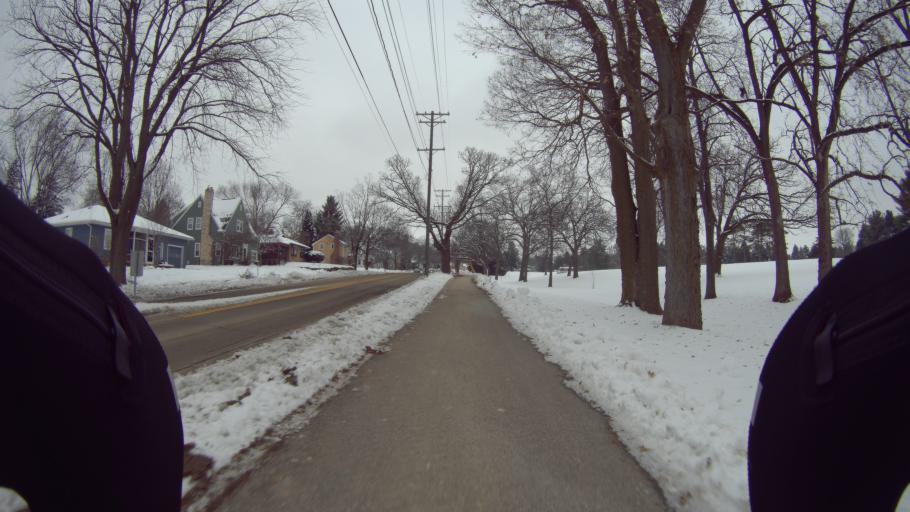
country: US
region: Wisconsin
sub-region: Dane County
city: Shorewood Hills
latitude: 43.0584
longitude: -89.4387
